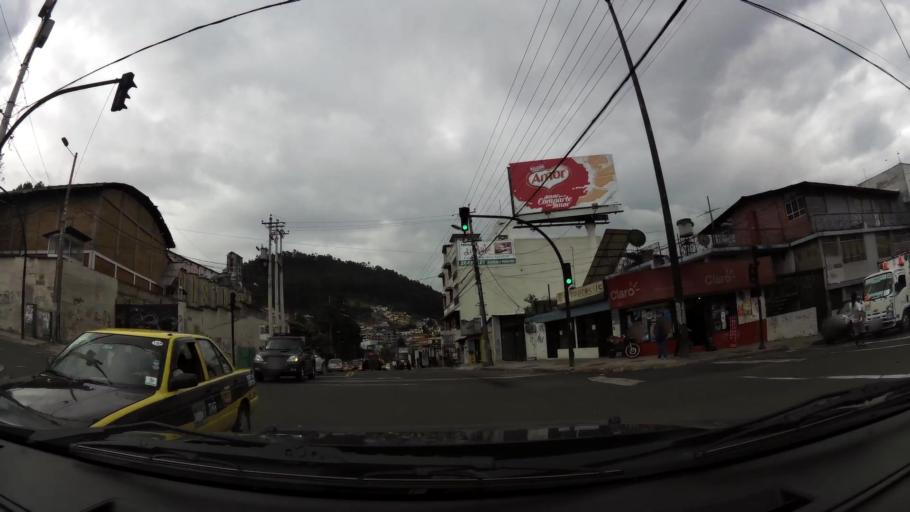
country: EC
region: Pichincha
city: Quito
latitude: -0.2391
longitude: -78.5234
